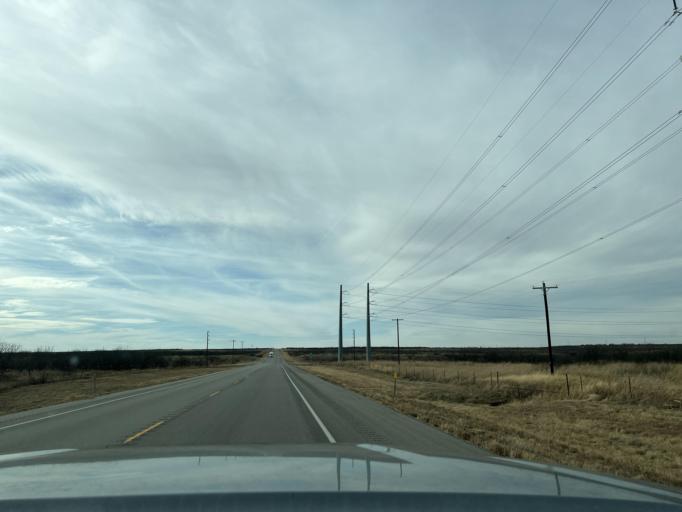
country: US
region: Texas
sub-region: Jones County
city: Anson
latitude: 32.7504
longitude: -99.6503
